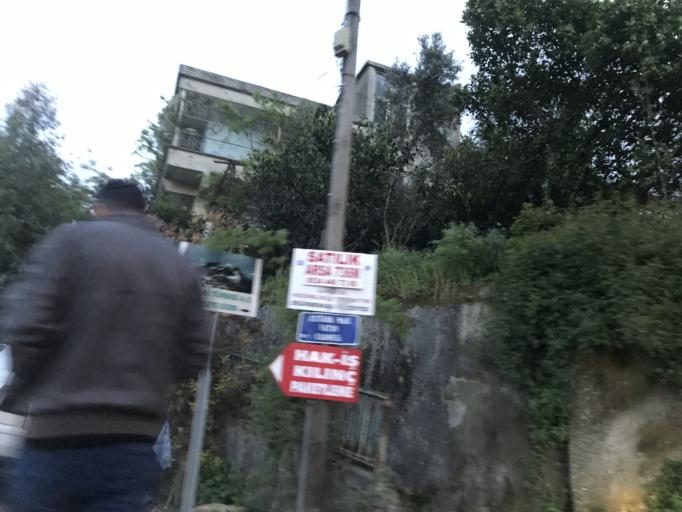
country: TR
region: Hatay
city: Uzunbag
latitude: 36.1327
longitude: 36.0414
